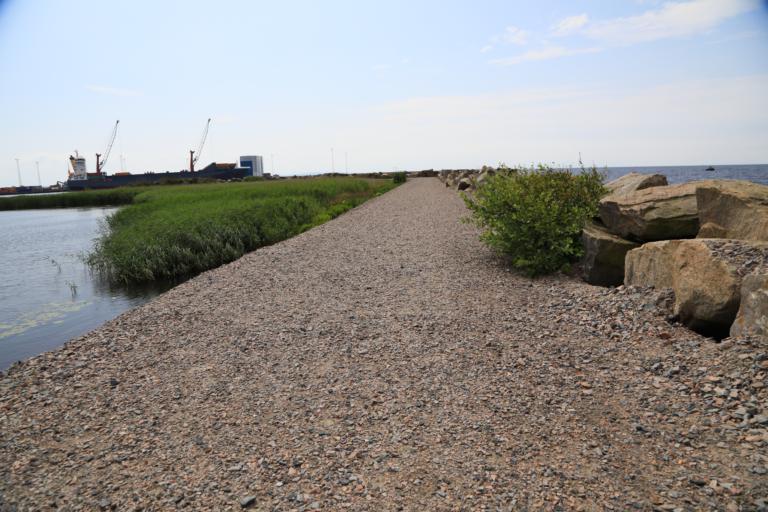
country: SE
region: Halland
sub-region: Halmstads Kommun
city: Halmstad
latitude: 56.6564
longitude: 12.8472
